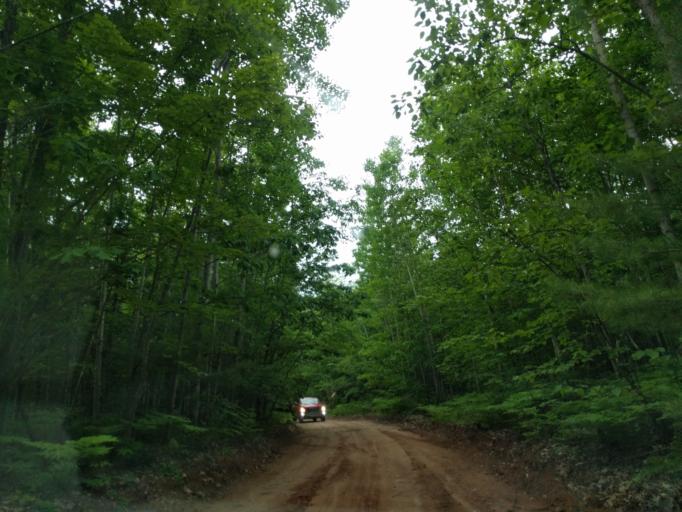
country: US
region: Michigan
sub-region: Marquette County
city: Trowbridge Park
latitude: 46.6080
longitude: -87.5081
